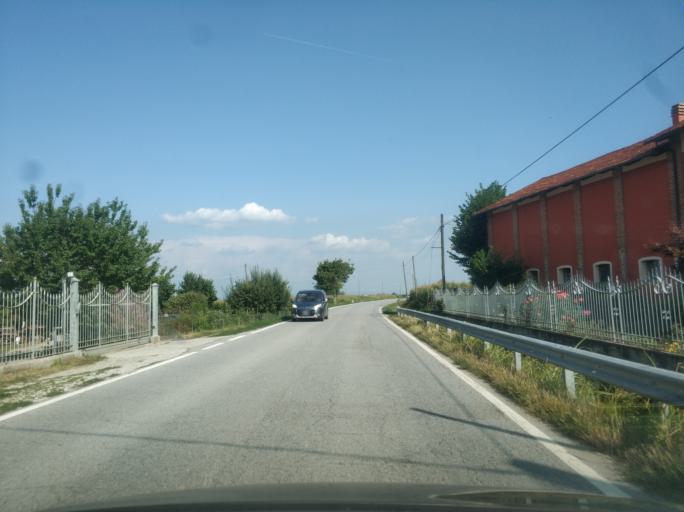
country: IT
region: Piedmont
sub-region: Provincia di Cuneo
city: Centallo
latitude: 44.5370
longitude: 7.6198
